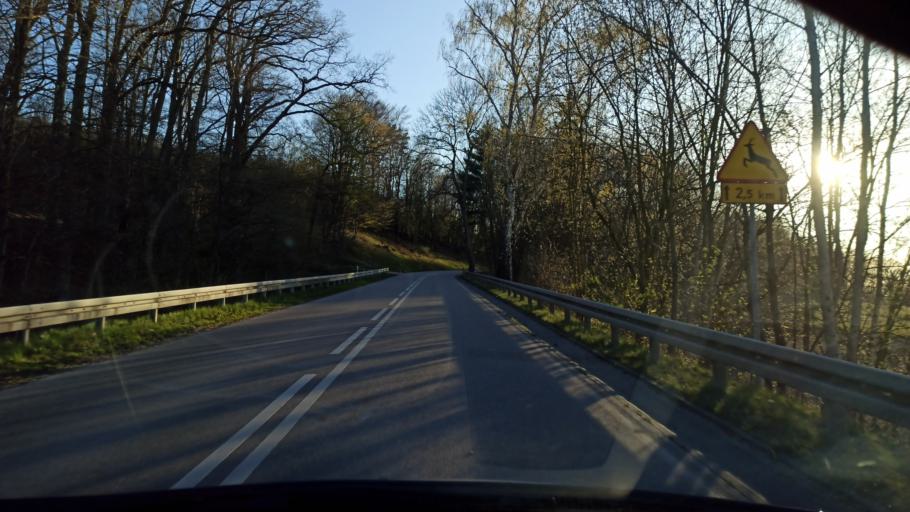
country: PL
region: Warmian-Masurian Voivodeship
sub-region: Powiat elblaski
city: Tolkmicko
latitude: 54.2925
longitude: 19.4786
